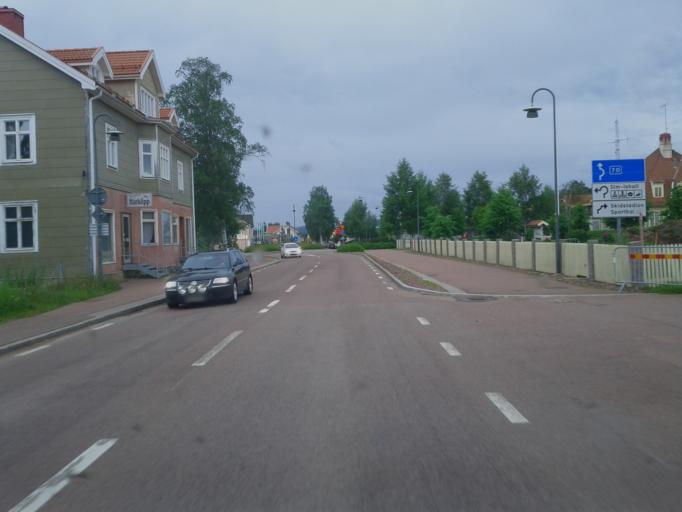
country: SE
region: Dalarna
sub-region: Alvdalens Kommun
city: AElvdalen
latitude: 61.2268
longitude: 14.0404
